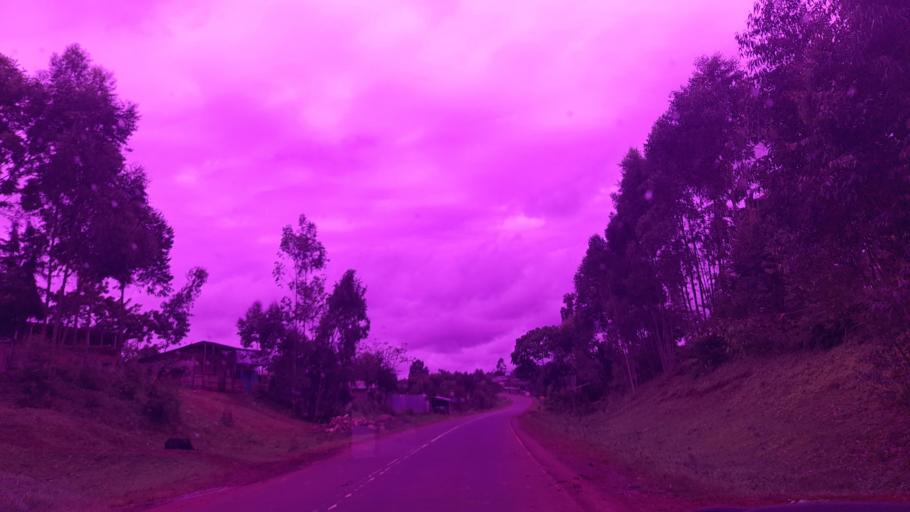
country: ET
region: Southern Nations, Nationalities, and People's Region
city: Bonga
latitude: 7.3006
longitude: 35.9916
